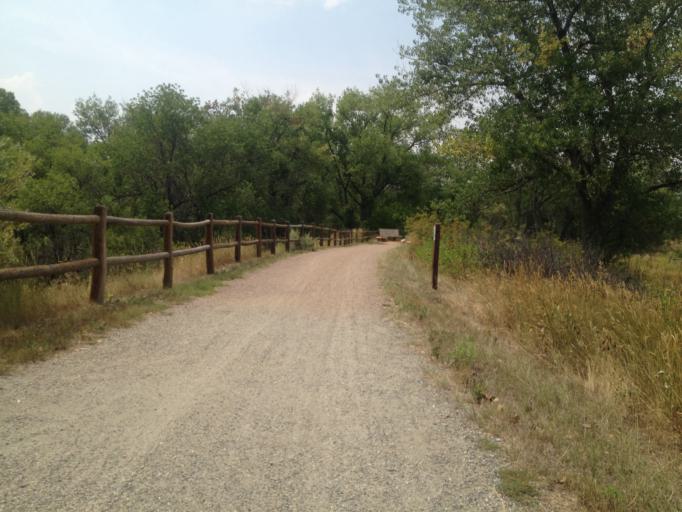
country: US
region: Colorado
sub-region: Boulder County
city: Superior
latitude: 39.9483
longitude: -105.1742
